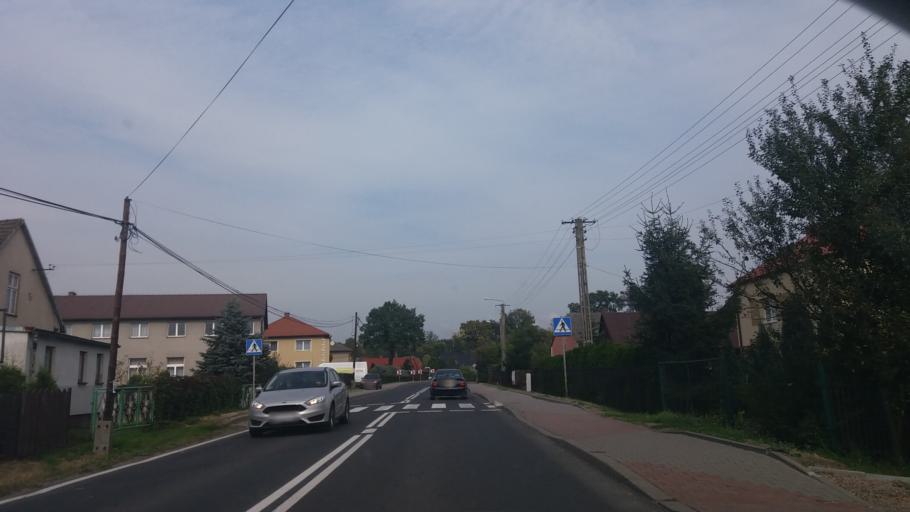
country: PL
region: Lesser Poland Voivodeship
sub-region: Powiat chrzanowski
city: Babice
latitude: 50.0509
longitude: 19.4492
